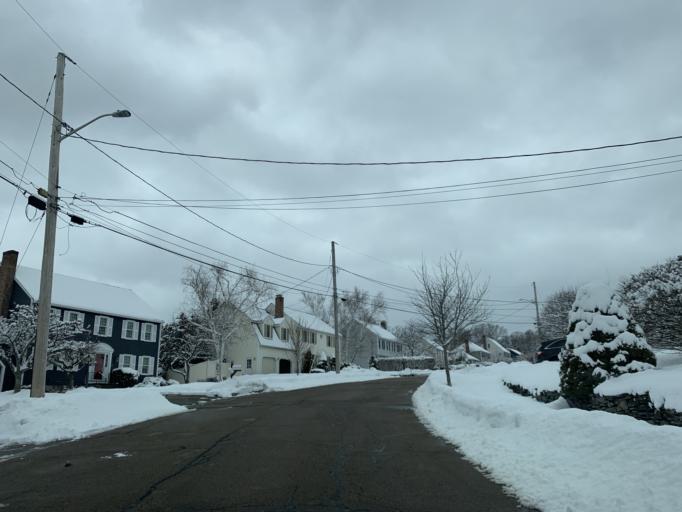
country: US
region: Massachusetts
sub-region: Norfolk County
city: Norwood
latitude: 42.1696
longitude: -71.1769
